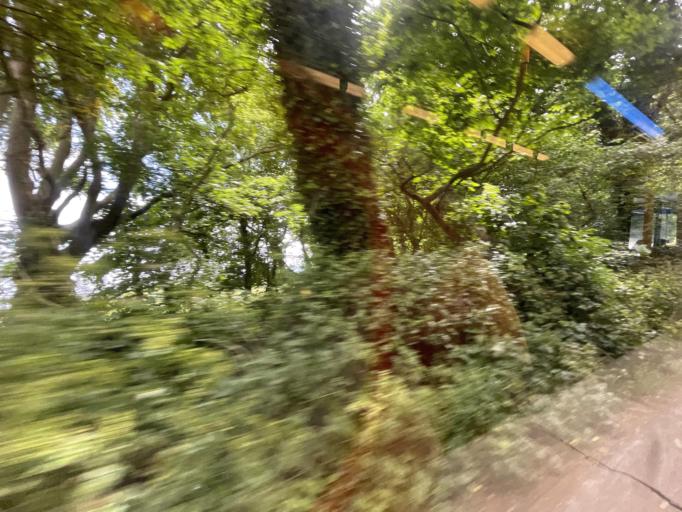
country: GB
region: Wales
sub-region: Anglesey
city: Beaumaris
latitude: 53.2702
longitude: -4.1130
